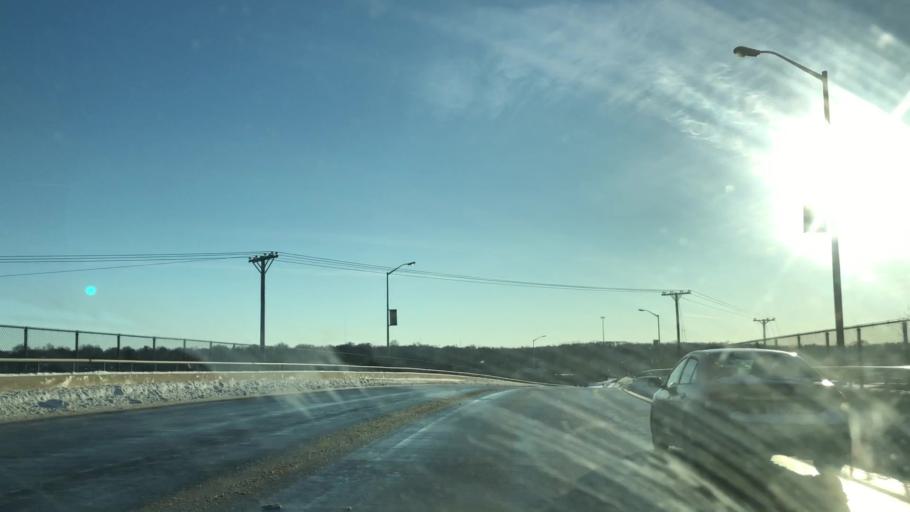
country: US
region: Iowa
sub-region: Marshall County
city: Marshalltown
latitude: 42.0410
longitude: -92.9185
